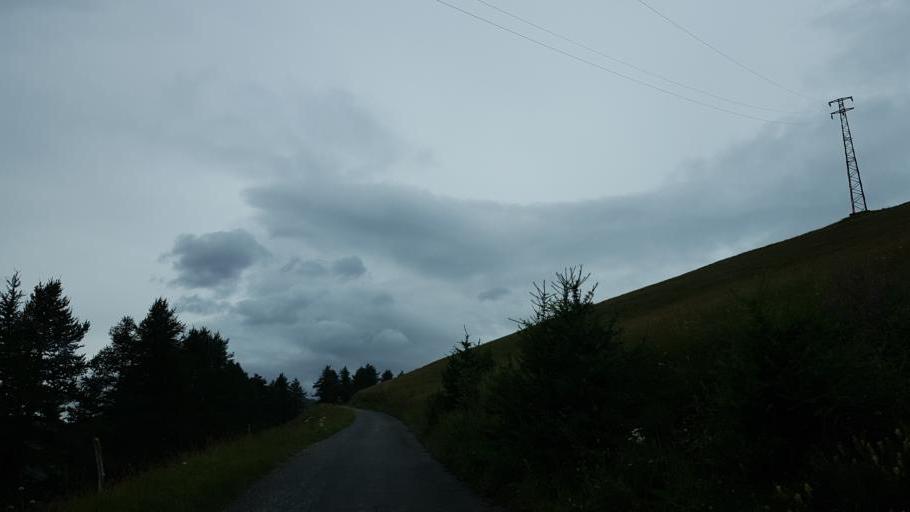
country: IT
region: Piedmont
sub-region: Provincia di Cuneo
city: Serre
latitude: 44.5322
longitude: 7.1142
